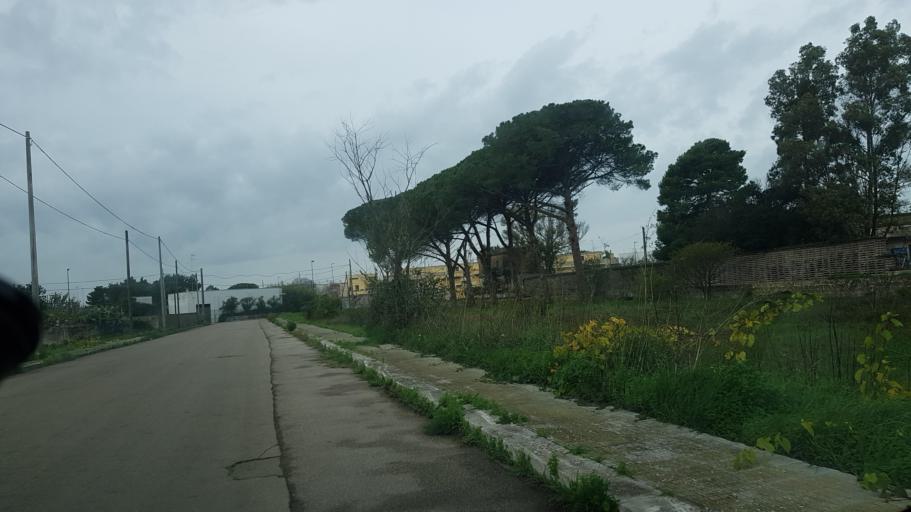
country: IT
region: Apulia
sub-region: Provincia di Lecce
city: Campi Salentina
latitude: 40.3933
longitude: 18.0197
